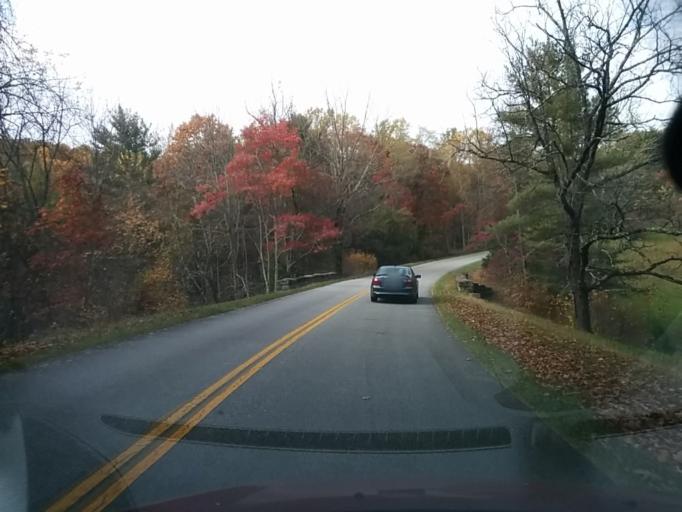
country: US
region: Virginia
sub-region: City of Buena Vista
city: Buena Vista
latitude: 37.7981
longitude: -79.2180
